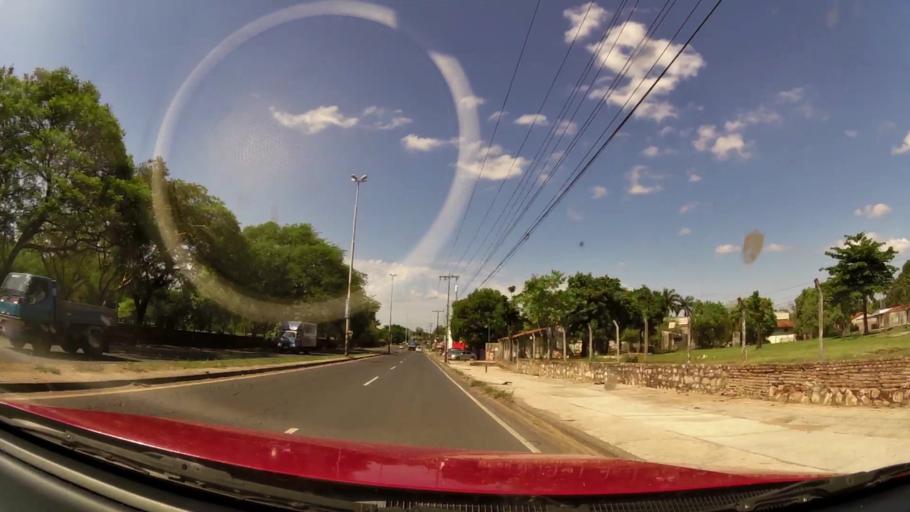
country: PY
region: Central
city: Colonia Mariano Roque Alonso
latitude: -25.2539
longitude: -57.5609
